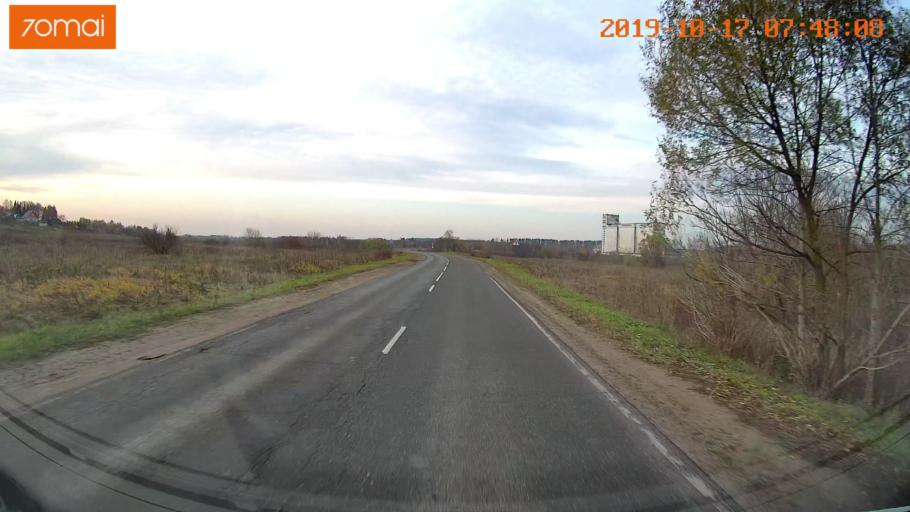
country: RU
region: Vladimir
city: Yur'yev-Pol'skiy
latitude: 56.4829
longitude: 39.6775
